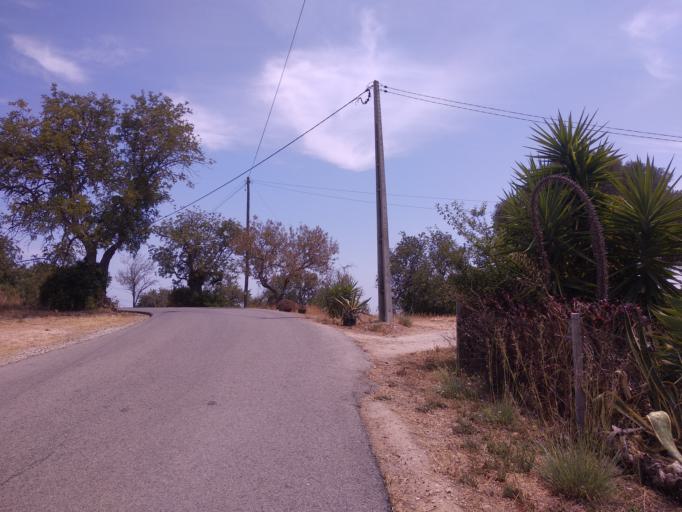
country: PT
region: Faro
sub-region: Loule
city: Almancil
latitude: 37.0774
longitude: -7.9986
